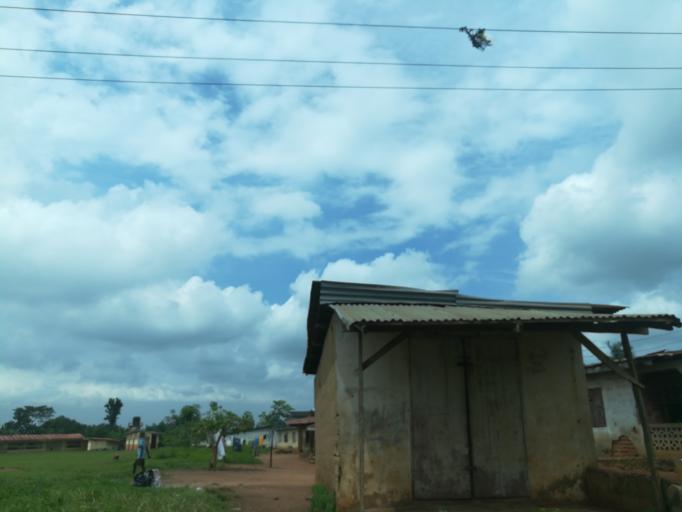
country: NG
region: Lagos
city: Ejirin
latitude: 6.6415
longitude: 3.7116
